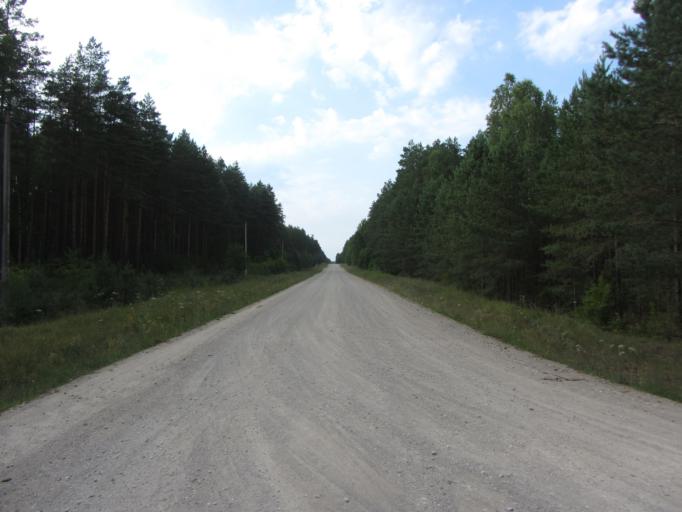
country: BY
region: Grodnenskaya
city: Sapotskin
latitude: 53.9526
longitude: 23.6706
